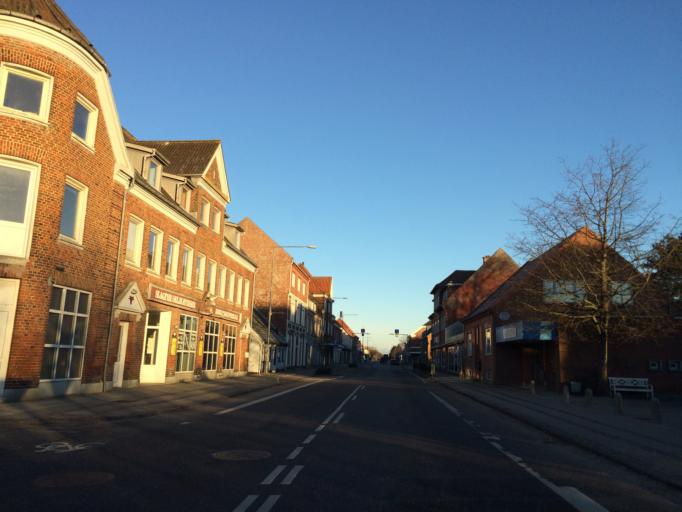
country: DK
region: Central Jutland
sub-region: Holstebro Kommune
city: Ulfborg
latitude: 56.3427
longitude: 8.3440
